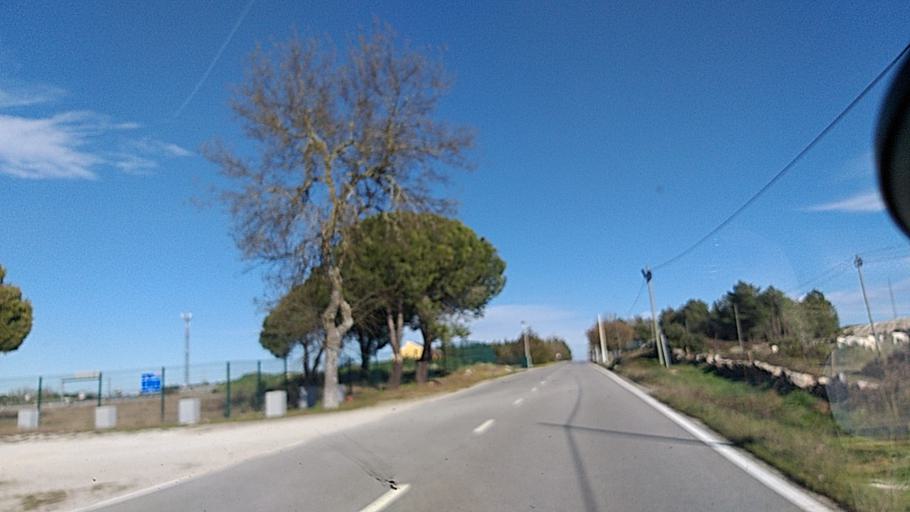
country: ES
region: Castille and Leon
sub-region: Provincia de Salamanca
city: Fuentes de Onoro
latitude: 40.6161
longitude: -6.8607
